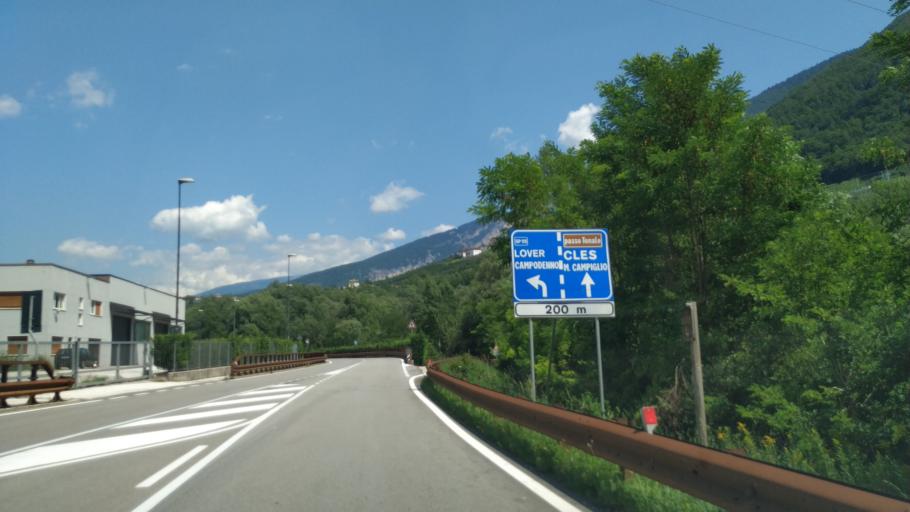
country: IT
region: Trentino-Alto Adige
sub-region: Provincia di Trento
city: Spormaggiore
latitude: 46.2410
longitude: 11.0575
